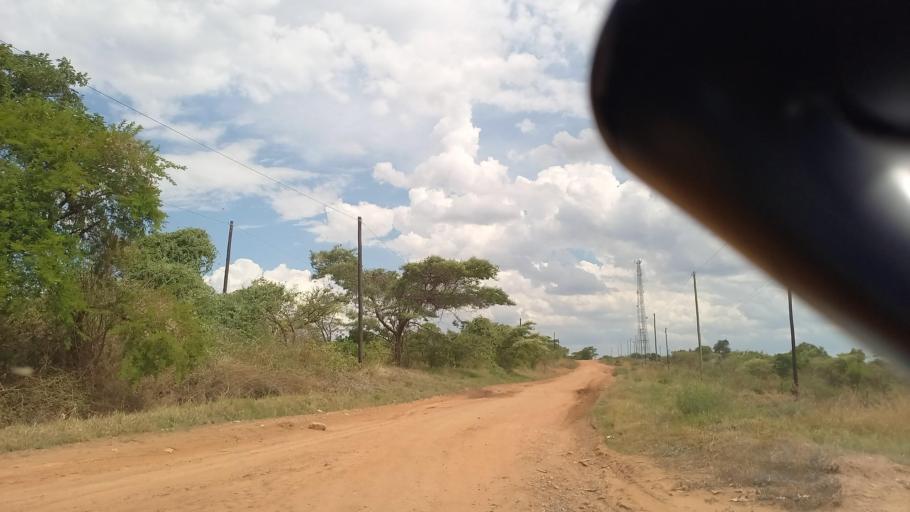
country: ZM
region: Southern
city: Nakambala
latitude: -16.0328
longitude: 27.9694
